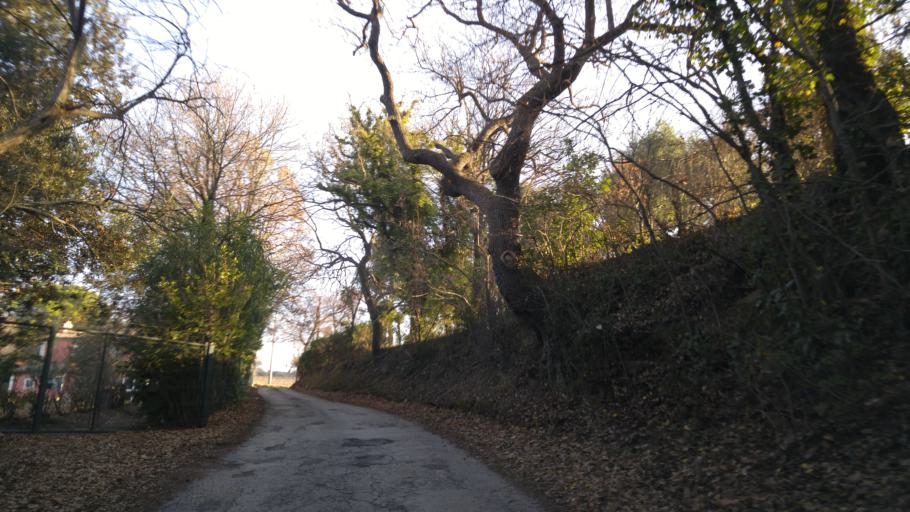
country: IT
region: The Marches
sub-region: Provincia di Pesaro e Urbino
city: Fenile
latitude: 43.8648
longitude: 12.9488
